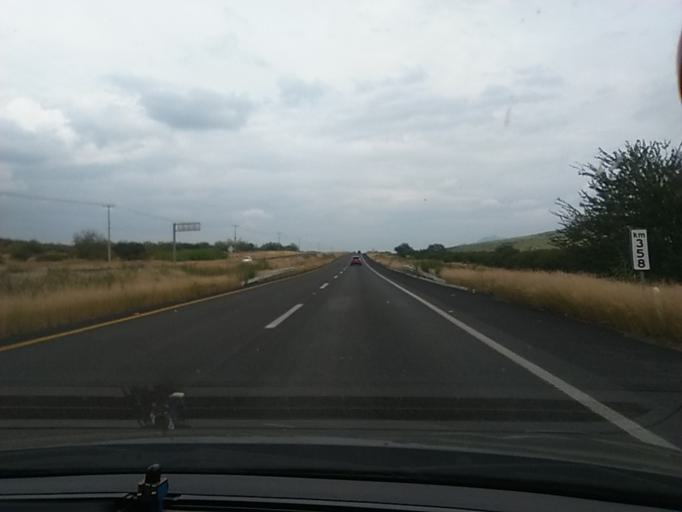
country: MX
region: Michoacan
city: Ecuandureo
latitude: 20.1741
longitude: -102.1700
